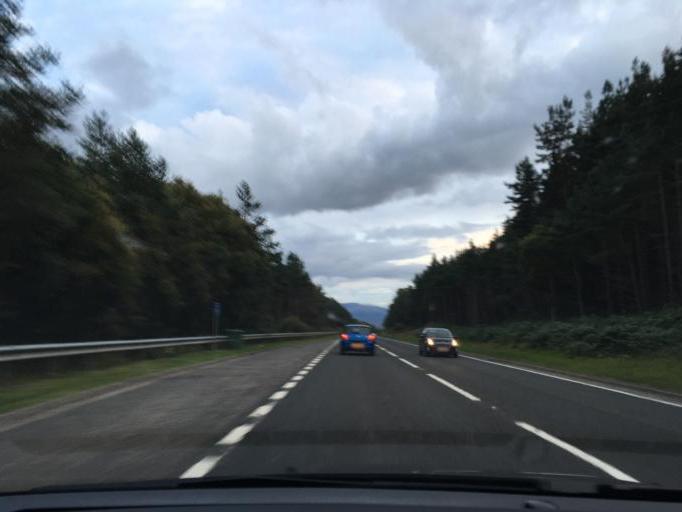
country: GB
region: Scotland
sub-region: Highland
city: Aviemore
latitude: 57.2552
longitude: -3.8082
